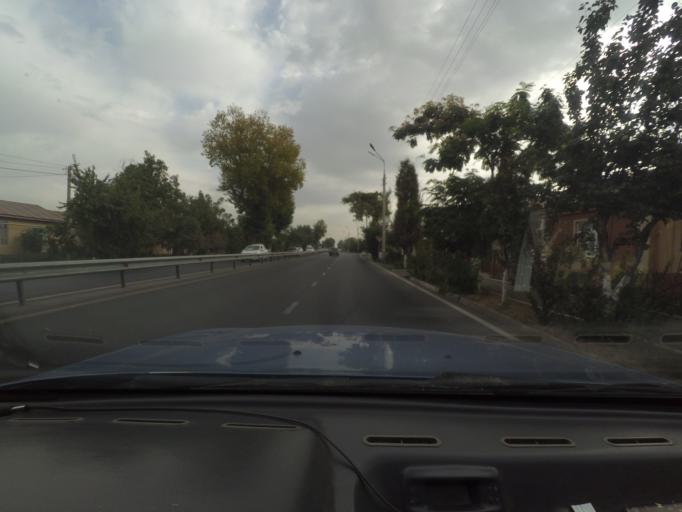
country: UZ
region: Toshkent
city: Salor
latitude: 41.3688
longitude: 69.4210
